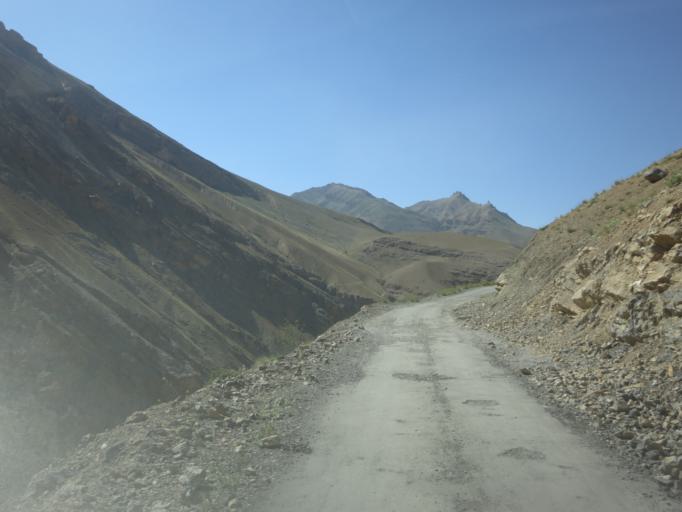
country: IN
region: Himachal Pradesh
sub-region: Kulu
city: Manali
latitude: 32.3164
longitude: 78.0025
